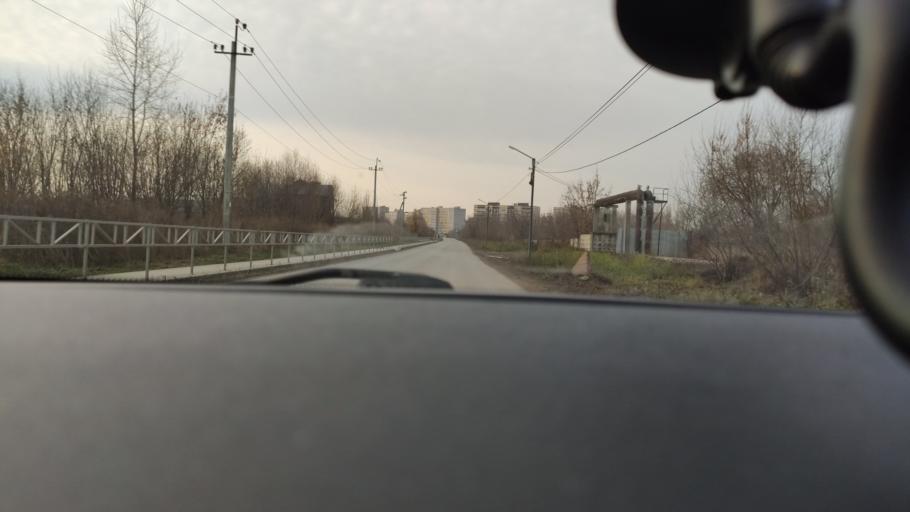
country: RU
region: Perm
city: Kondratovo
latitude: 57.9834
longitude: 56.1153
